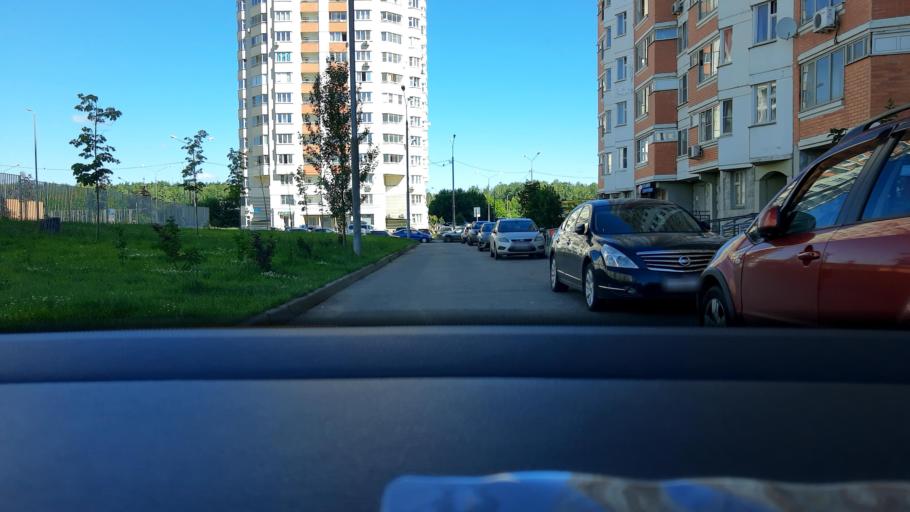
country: RU
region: Moscow
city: Vostochnyy
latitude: 55.8210
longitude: 37.8755
